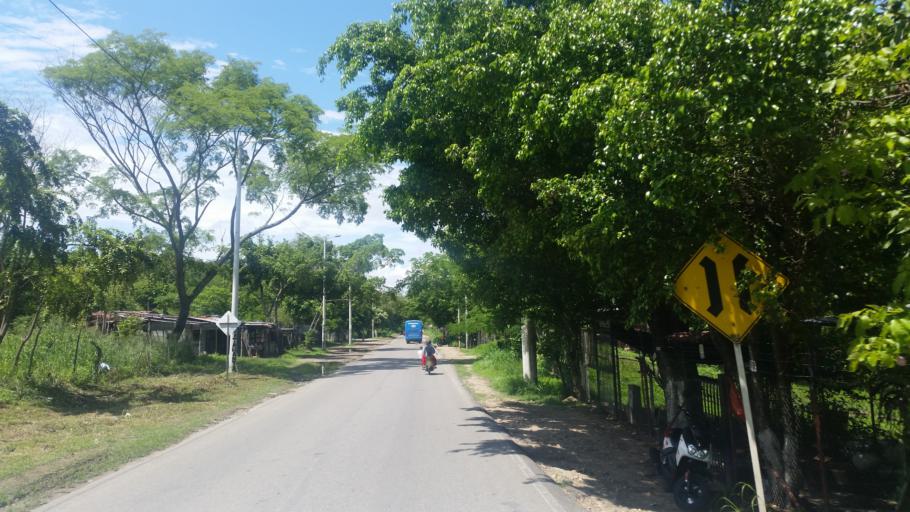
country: CO
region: Huila
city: Neiva
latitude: 2.9844
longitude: -75.2793
